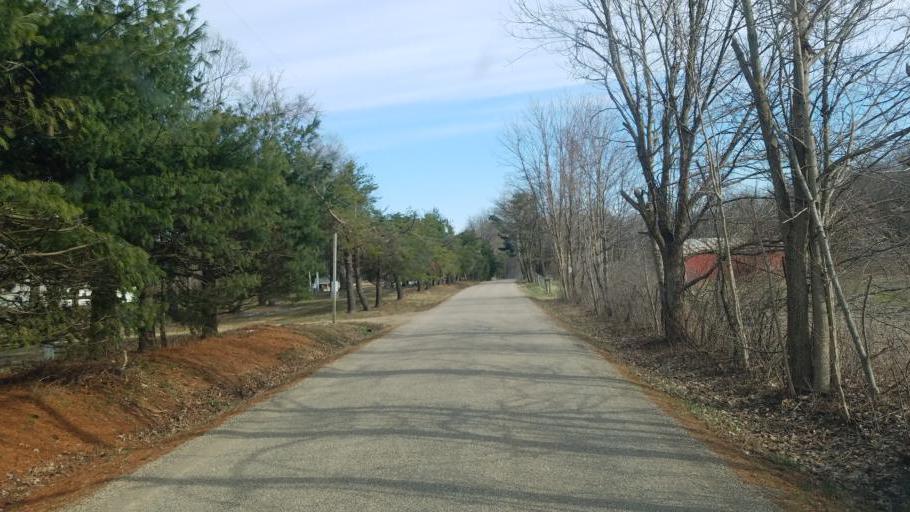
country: US
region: Ohio
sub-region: Sandusky County
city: Bellville
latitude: 40.5786
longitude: -82.5797
